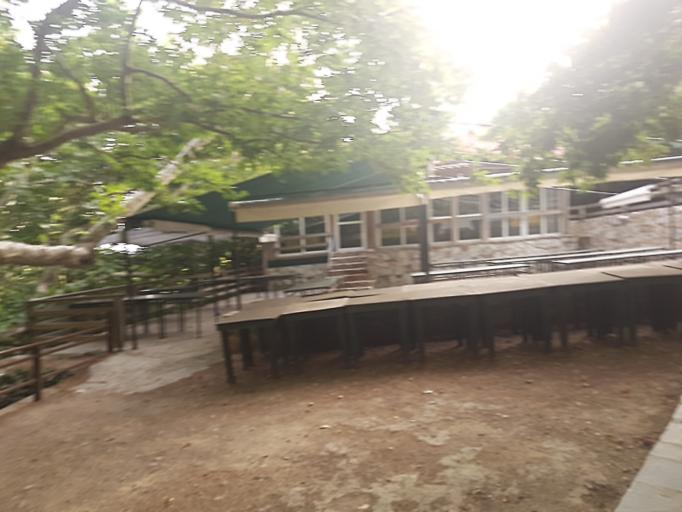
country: GR
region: Central Greece
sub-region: Nomos Evvoias
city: Yimnon
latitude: 38.5608
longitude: 23.8440
